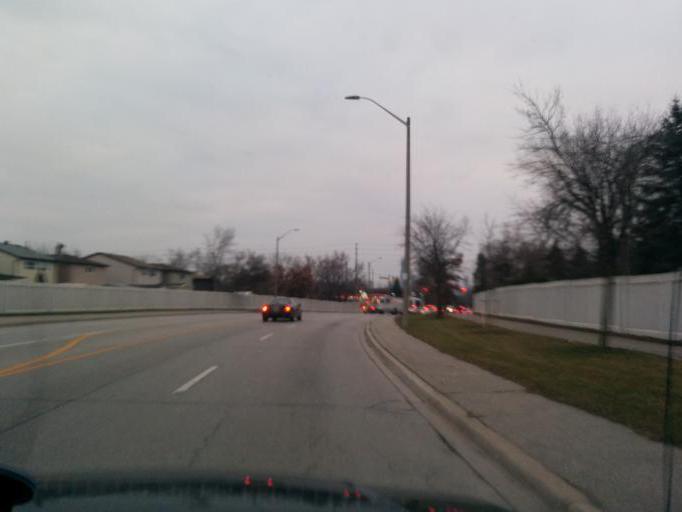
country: CA
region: Ontario
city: Mississauga
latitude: 43.6118
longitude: -79.6205
